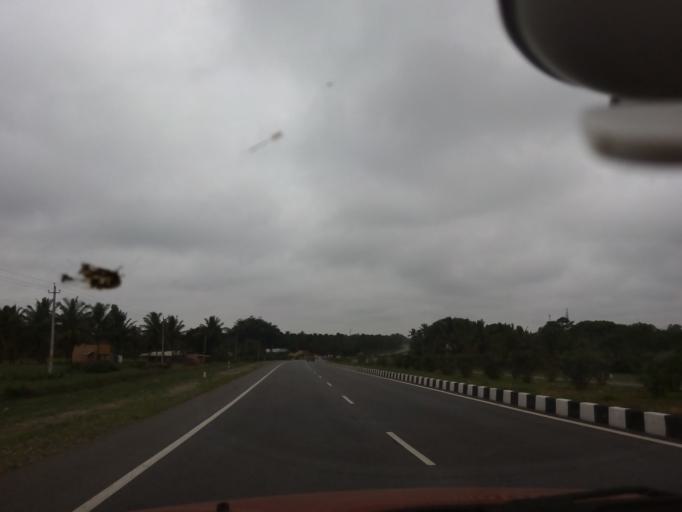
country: IN
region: Karnataka
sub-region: Hassan
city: Shravanabelagola
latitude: 12.9282
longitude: 76.5165
